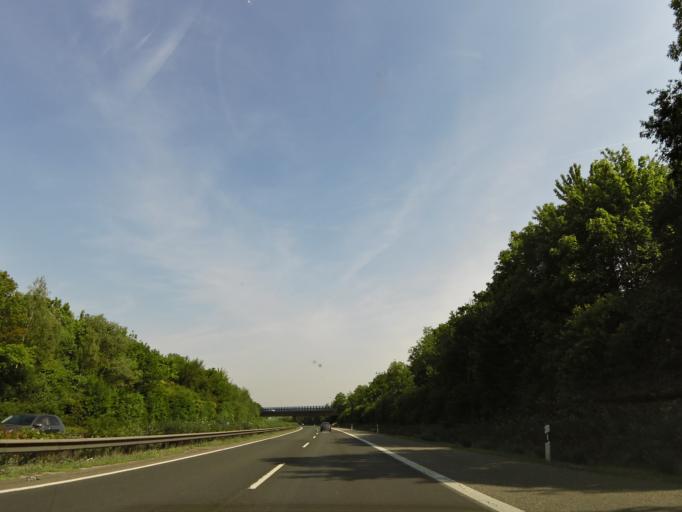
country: DE
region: Rheinland-Pfalz
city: Alzey
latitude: 49.7406
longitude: 8.1383
